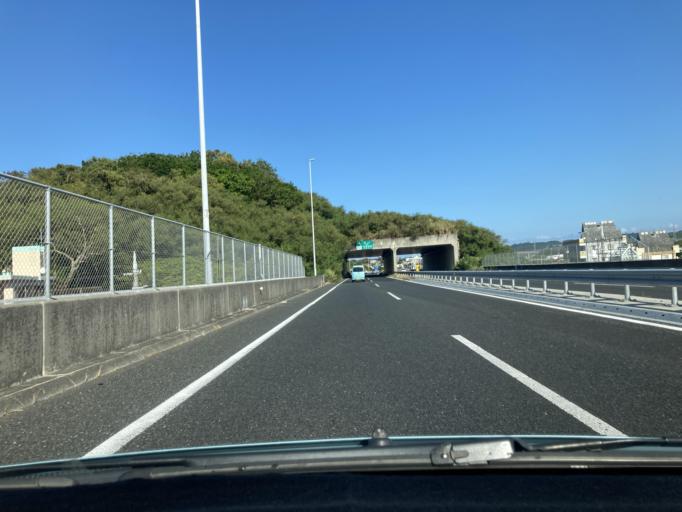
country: JP
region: Okinawa
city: Tomigusuku
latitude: 26.1801
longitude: 127.7163
